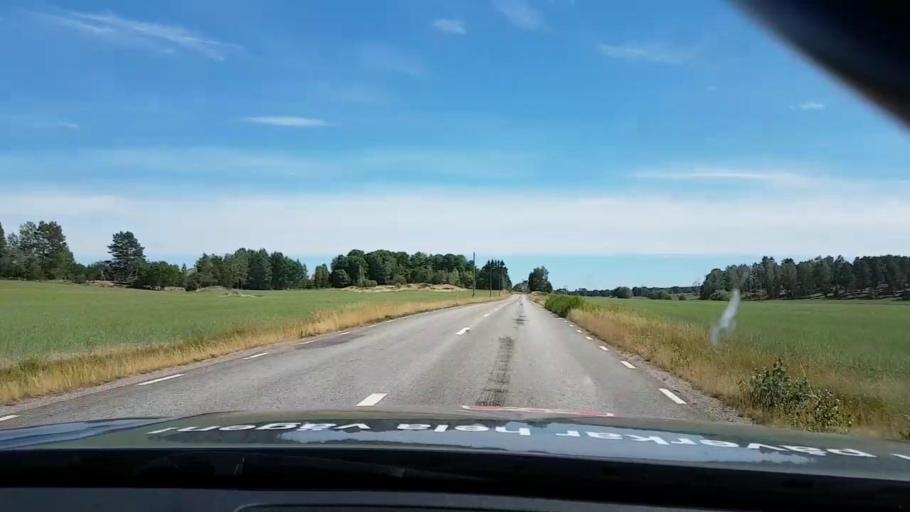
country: SE
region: Kalmar
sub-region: Vasterviks Kommun
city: Forserum
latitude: 57.9386
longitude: 16.5003
